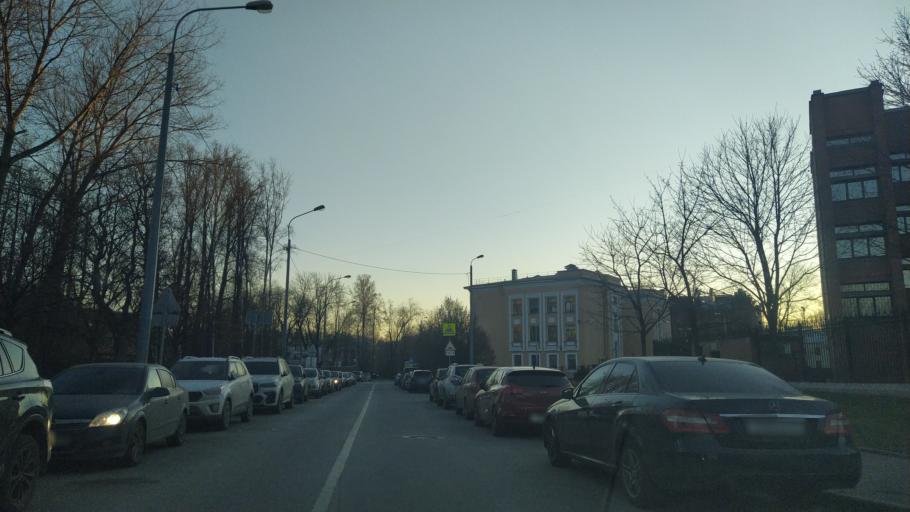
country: RU
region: St.-Petersburg
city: Novaya Derevnya
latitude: 59.9734
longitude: 30.2758
